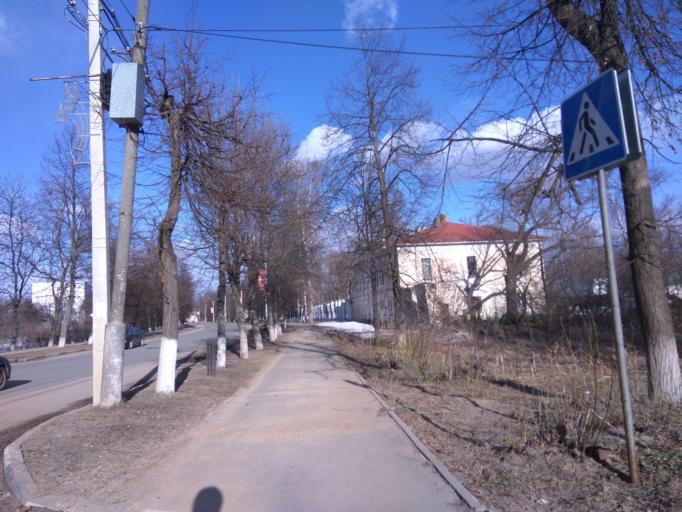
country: RU
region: Jaroslavl
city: Rostov
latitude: 57.1859
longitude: 39.4218
